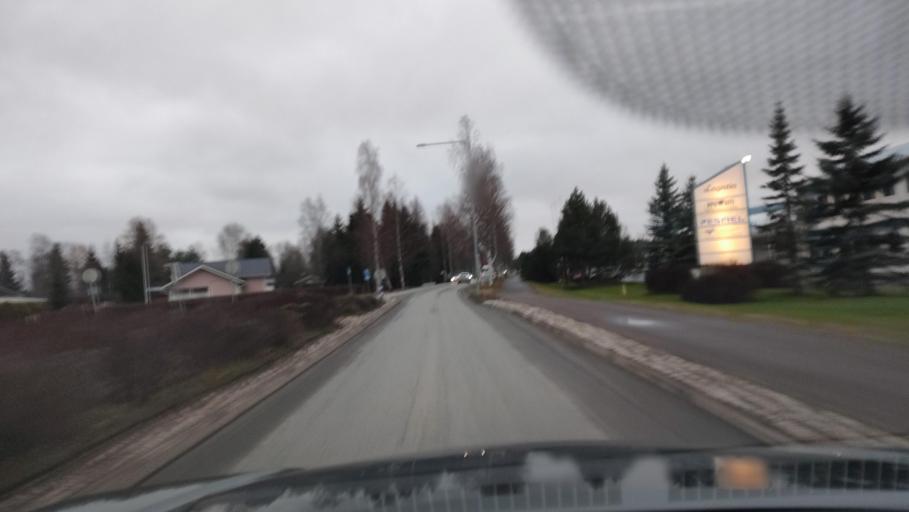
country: FI
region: Southern Ostrobothnia
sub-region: Suupohja
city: Kauhajoki
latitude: 62.4174
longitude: 22.1747
